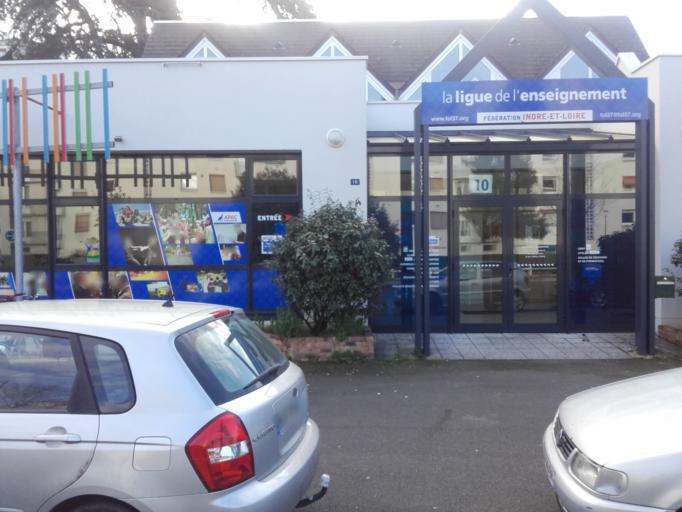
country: FR
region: Centre
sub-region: Departement d'Indre-et-Loire
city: Joue-les-Tours
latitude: 47.3566
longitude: 0.6660
